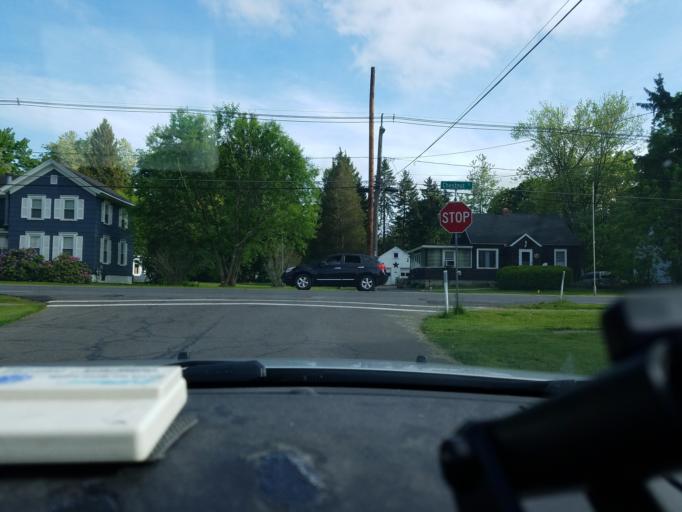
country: US
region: New York
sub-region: Onondaga County
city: North Syracuse
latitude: 43.1364
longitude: -76.1370
